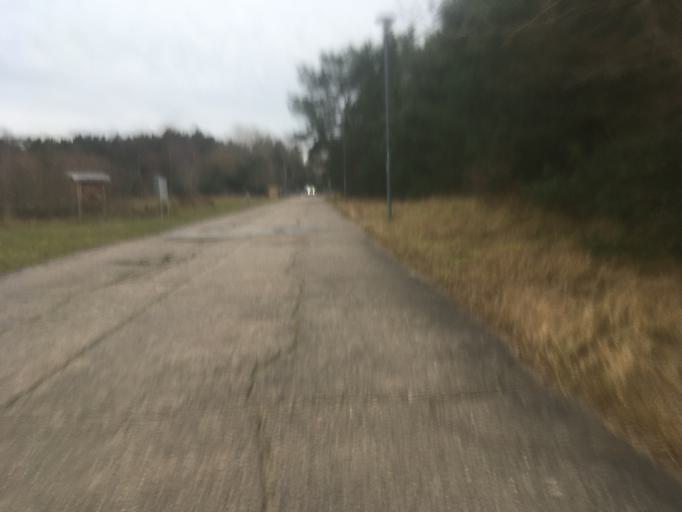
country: DE
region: Mecklenburg-Vorpommern
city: Ostseebad Binz
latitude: 54.4551
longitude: 13.5680
